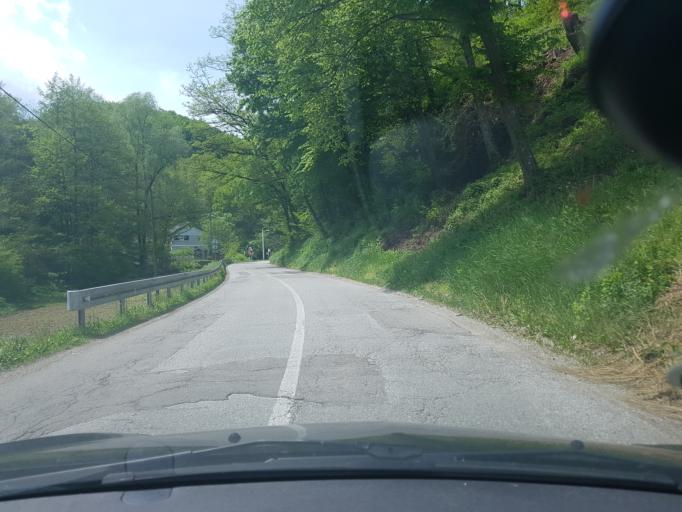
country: HR
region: Krapinsko-Zagorska
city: Pregrada
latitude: 46.1889
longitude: 15.7357
